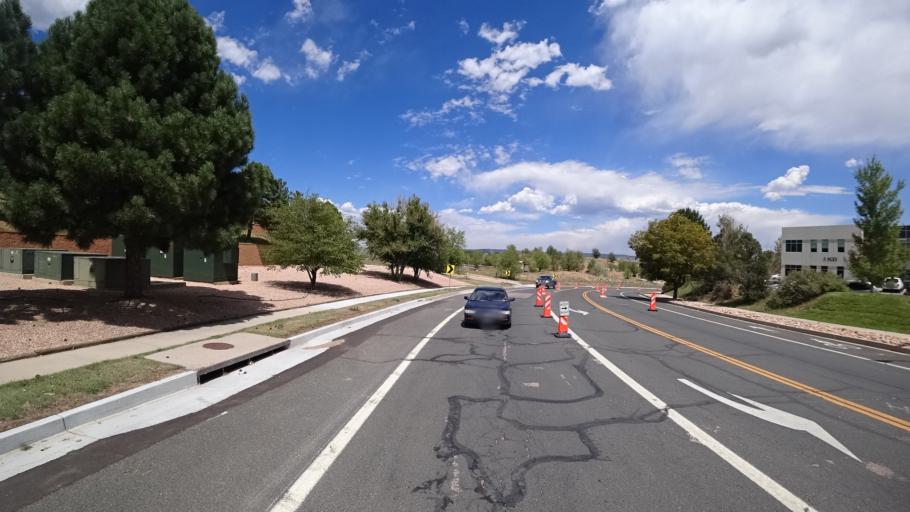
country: US
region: Colorado
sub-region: El Paso County
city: Stratmoor
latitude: 38.7890
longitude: -104.8041
